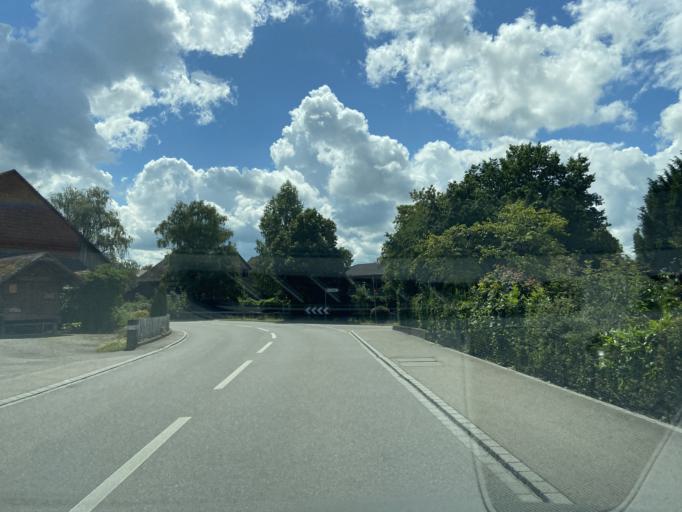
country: CH
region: Zurich
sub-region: Bezirk Winterthur
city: Wiesendangen / Wiesendangen (Dorf)
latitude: 47.5211
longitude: 8.7855
